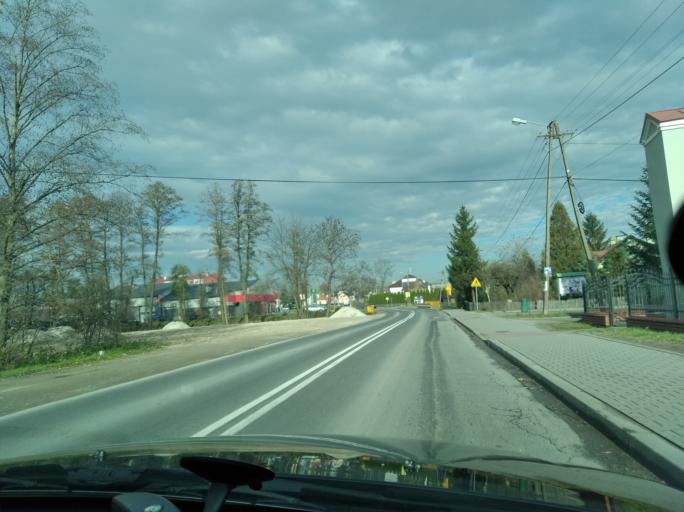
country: PL
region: Subcarpathian Voivodeship
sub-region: Powiat ropczycko-sedziszowski
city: Ostrow
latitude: 50.0967
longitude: 21.5937
